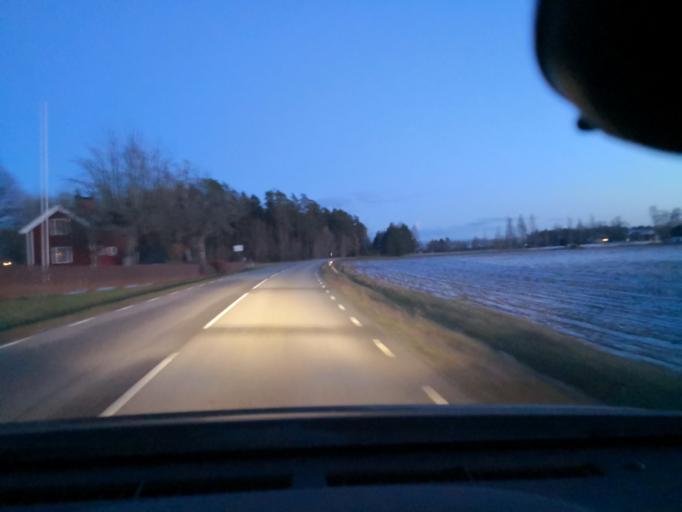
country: SE
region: Vaestmanland
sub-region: Sala Kommun
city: Sala
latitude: 59.8748
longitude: 16.7008
